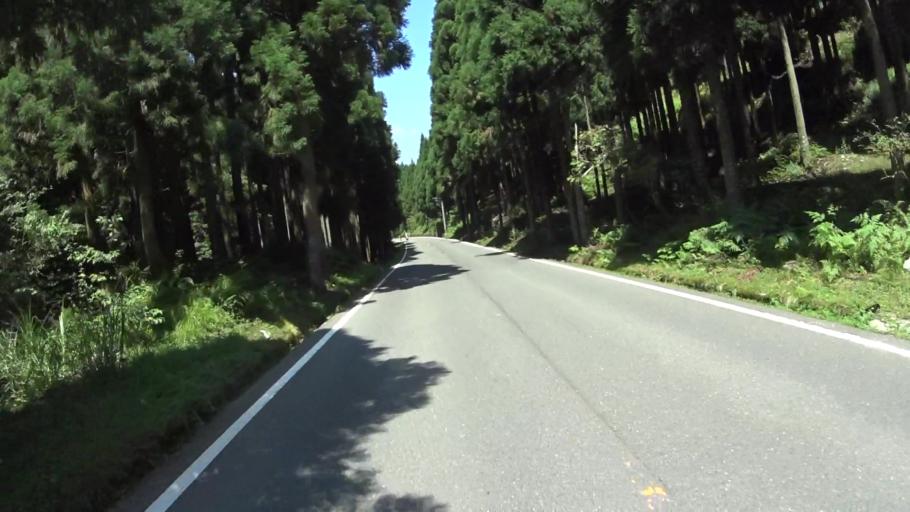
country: JP
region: Fukui
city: Obama
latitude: 35.3879
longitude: 135.9260
